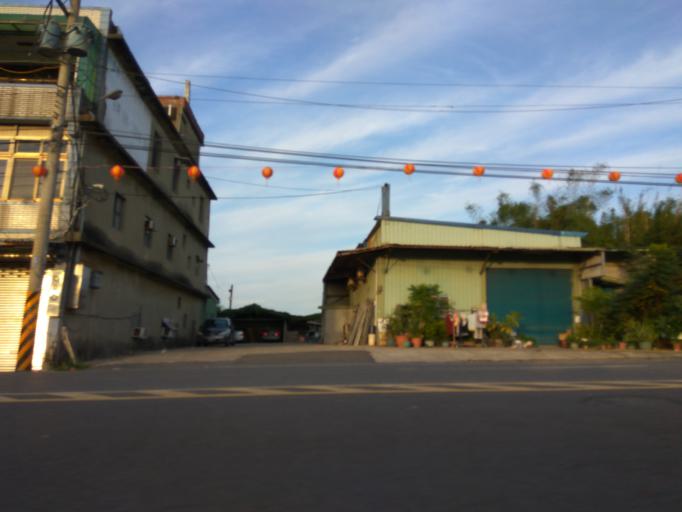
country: TW
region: Taiwan
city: Taoyuan City
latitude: 25.0016
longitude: 121.1548
